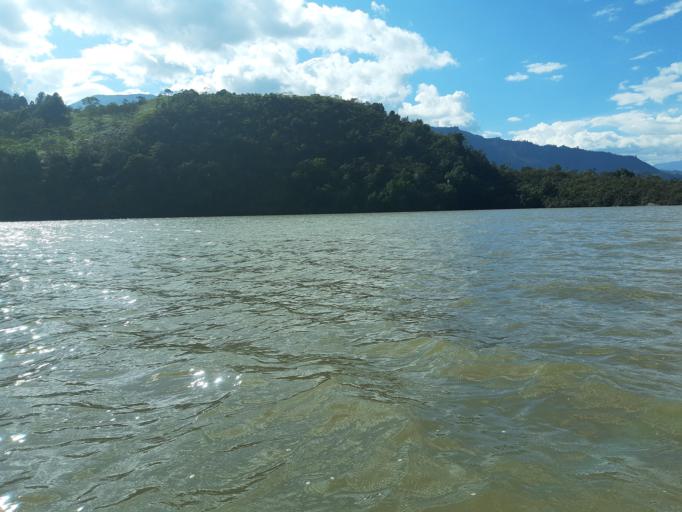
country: CO
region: Boyaca
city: Chivor
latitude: 4.9430
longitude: -73.3168
